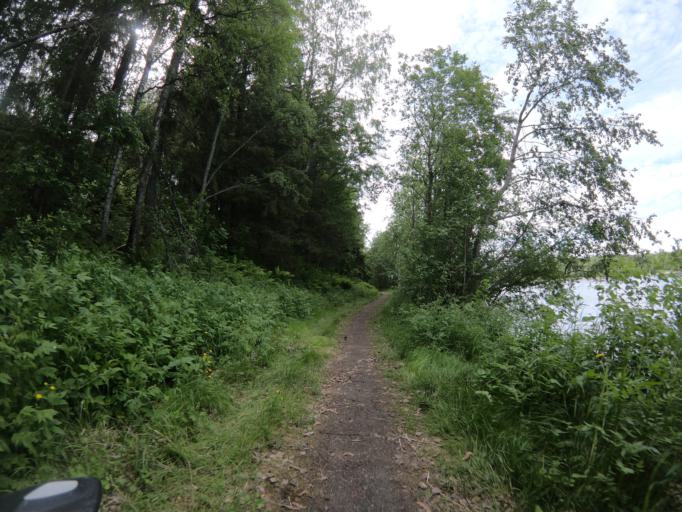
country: SE
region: Vaesterbotten
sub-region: Umea Kommun
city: Roback
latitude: 63.8210
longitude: 20.2176
